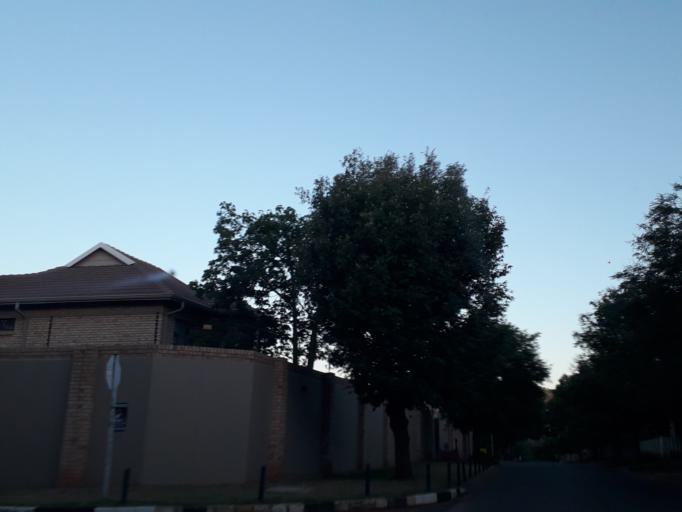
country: ZA
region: Gauteng
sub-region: City of Johannesburg Metropolitan Municipality
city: Roodepoort
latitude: -26.1345
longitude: 27.9399
